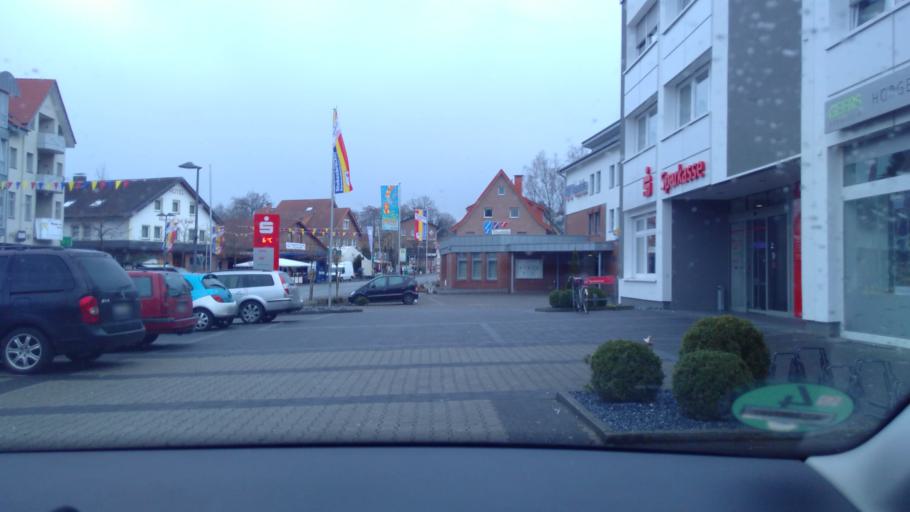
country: DE
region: North Rhine-Westphalia
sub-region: Regierungsbezirk Detmold
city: Oerlinghausen
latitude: 51.9119
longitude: 8.6566
